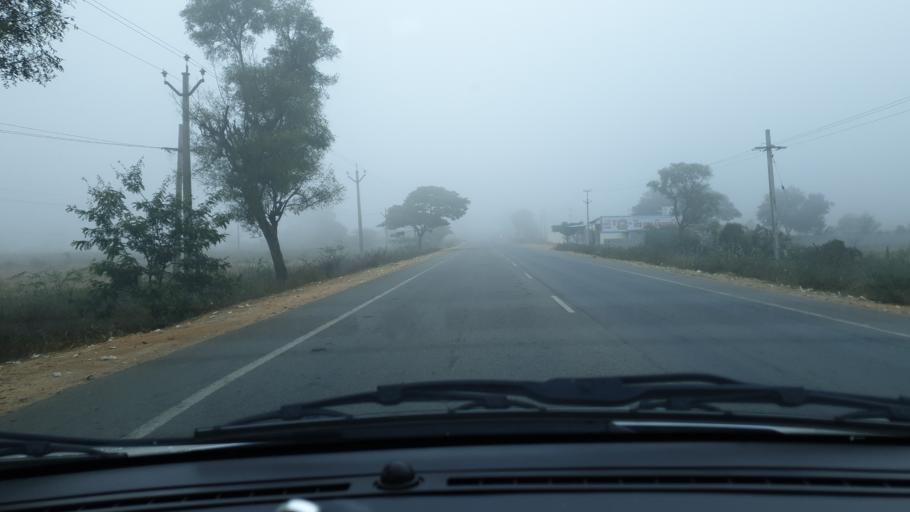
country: IN
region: Telangana
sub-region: Mahbubnagar
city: Nagar Karnul
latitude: 16.6643
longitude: 78.5613
